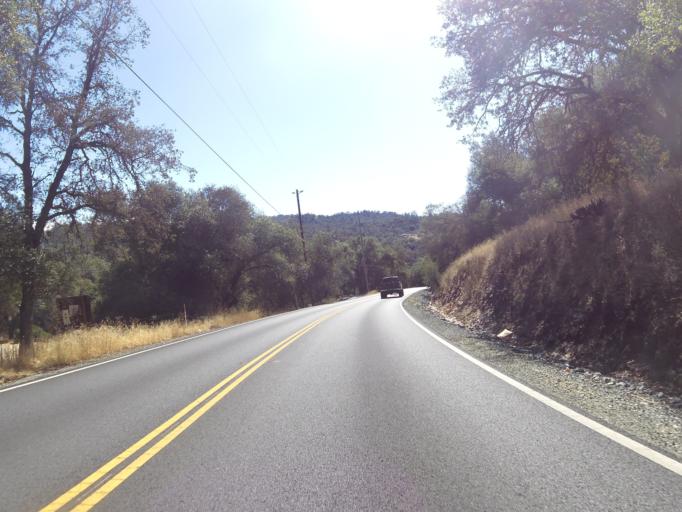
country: US
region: California
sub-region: El Dorado County
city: Deer Park
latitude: 38.5952
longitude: -120.8478
